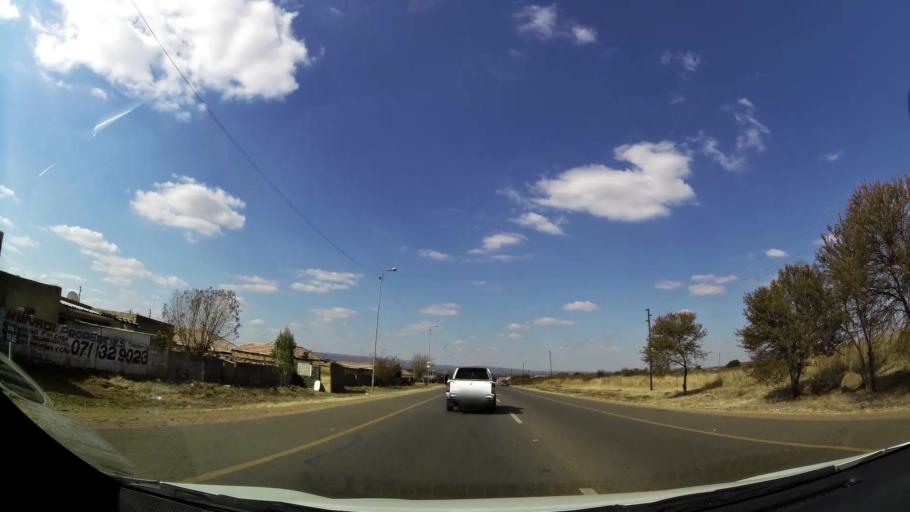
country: ZA
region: Gauteng
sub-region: City of Tshwane Metropolitan Municipality
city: Pretoria
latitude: -25.7473
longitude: 28.3575
